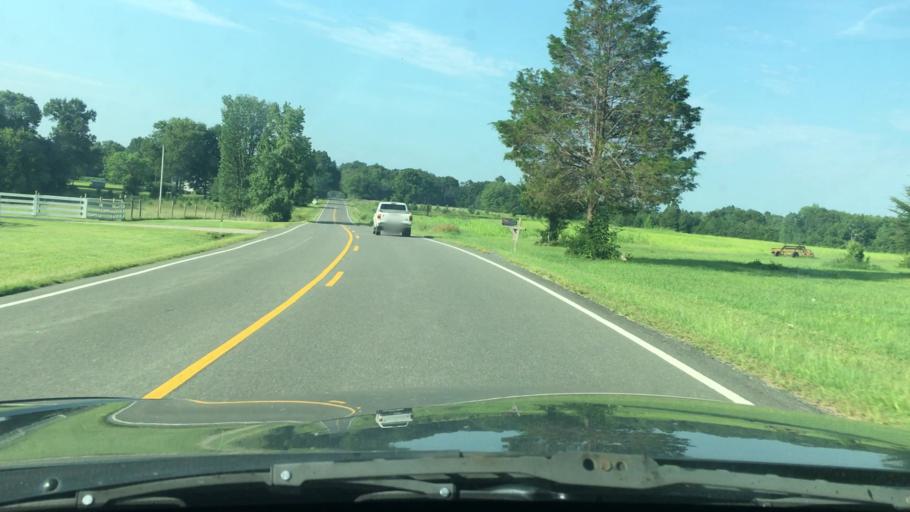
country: US
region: North Carolina
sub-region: Caswell County
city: Yanceyville
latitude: 36.3075
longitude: -79.3619
